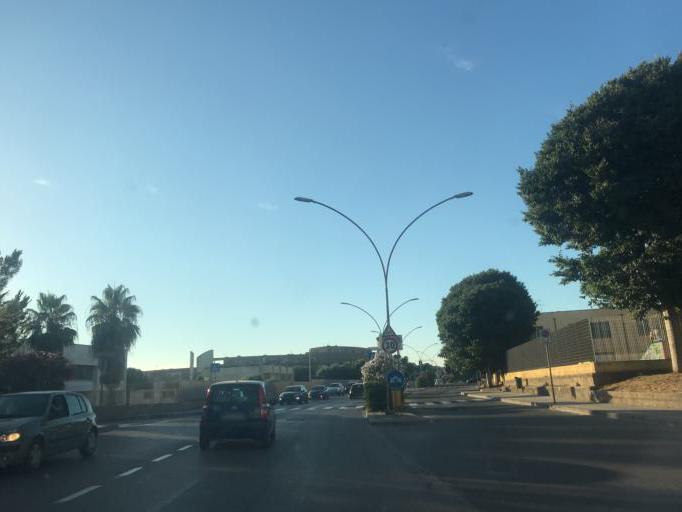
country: IT
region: Sardinia
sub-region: Provincia di Sassari
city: Alghero
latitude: 40.5772
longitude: 8.3198
